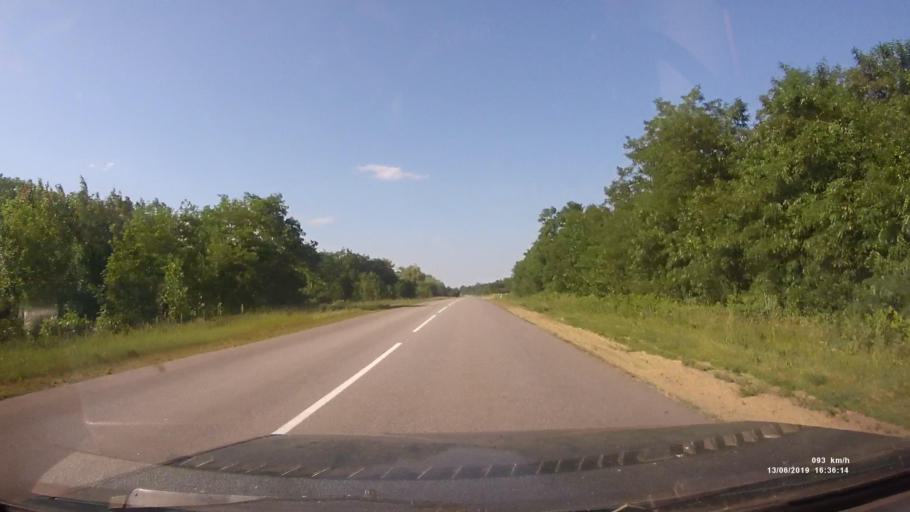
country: RU
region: Rostov
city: Kazanskaya
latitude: 49.8925
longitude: 41.3045
